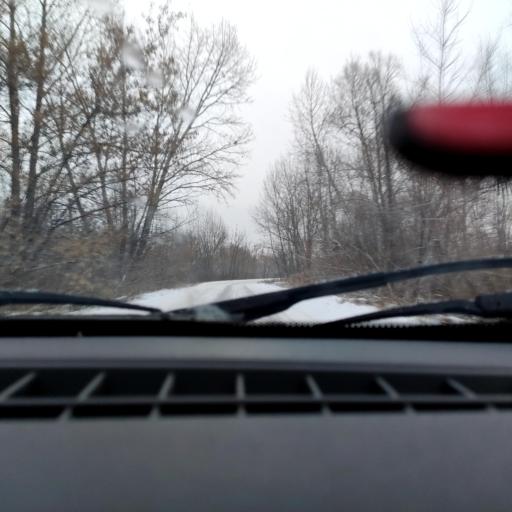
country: RU
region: Bashkortostan
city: Blagoveshchensk
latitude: 54.9052
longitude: 56.0117
